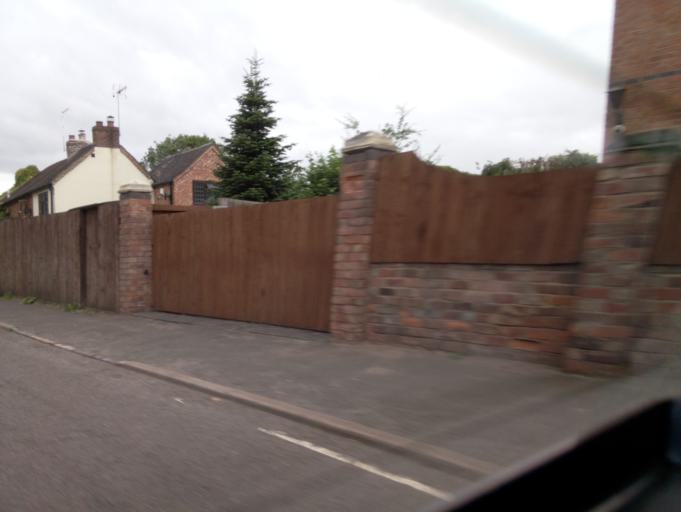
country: GB
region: England
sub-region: Worcestershire
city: Droitwich
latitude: 52.2991
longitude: -2.1072
